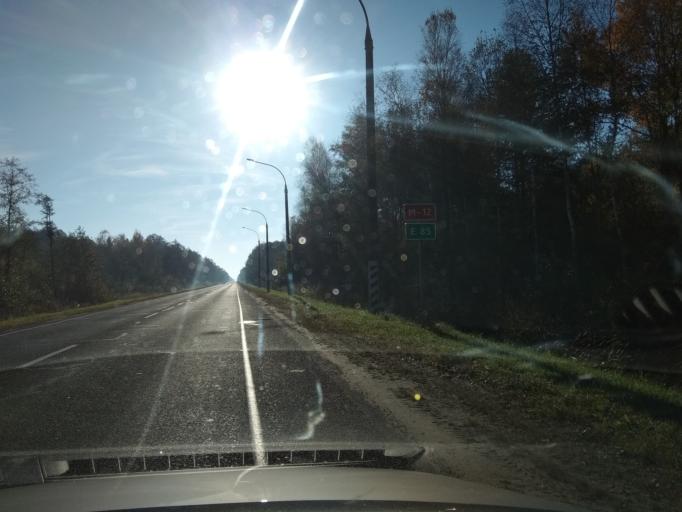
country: BY
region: Brest
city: Malaryta
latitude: 51.8904
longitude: 24.1432
